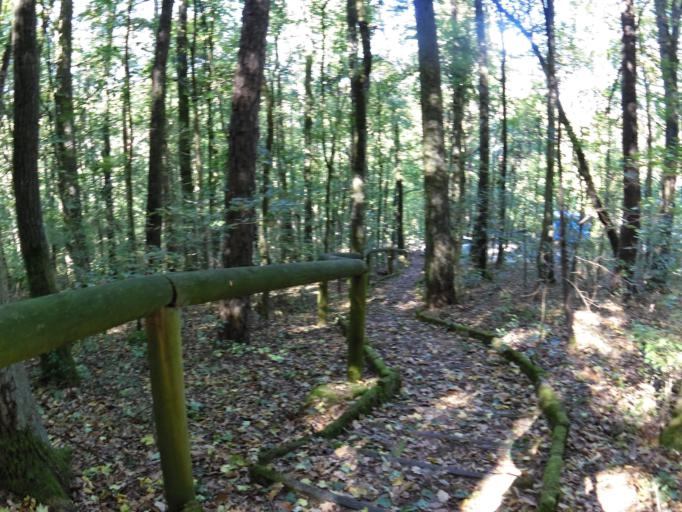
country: DE
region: Bavaria
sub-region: Regierungsbezirk Unterfranken
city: Reichenberg
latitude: 49.7438
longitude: 9.9325
